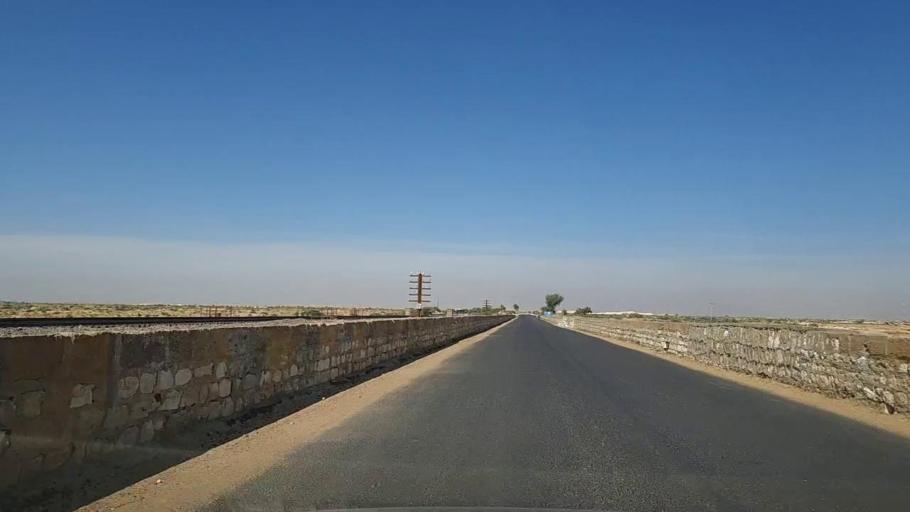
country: PK
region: Sindh
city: Kotri
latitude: 25.2994
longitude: 68.2036
